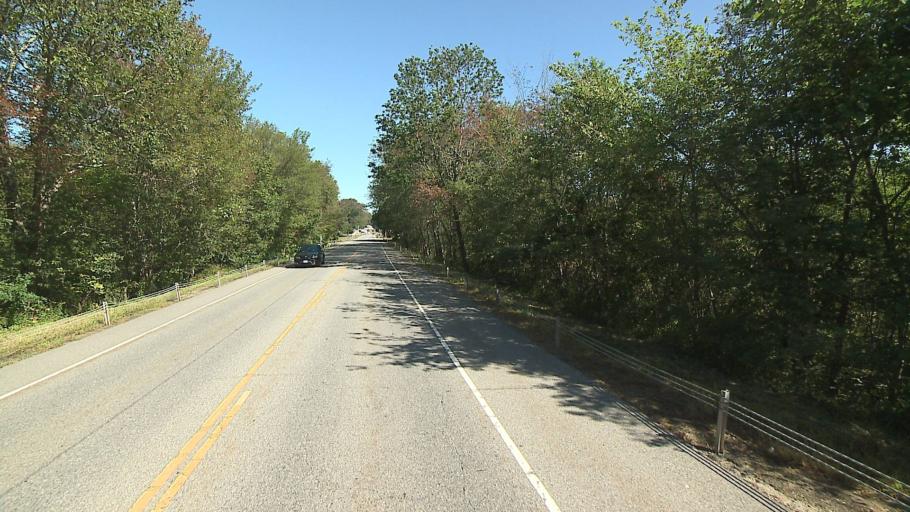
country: US
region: Connecticut
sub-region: Windham County
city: Moosup
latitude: 41.7066
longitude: -71.9052
